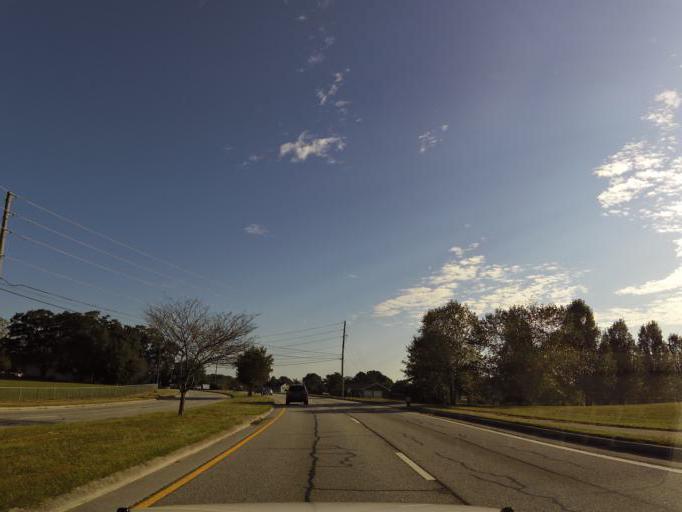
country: US
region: Georgia
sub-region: Cobb County
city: Marietta
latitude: 33.9321
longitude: -84.6311
